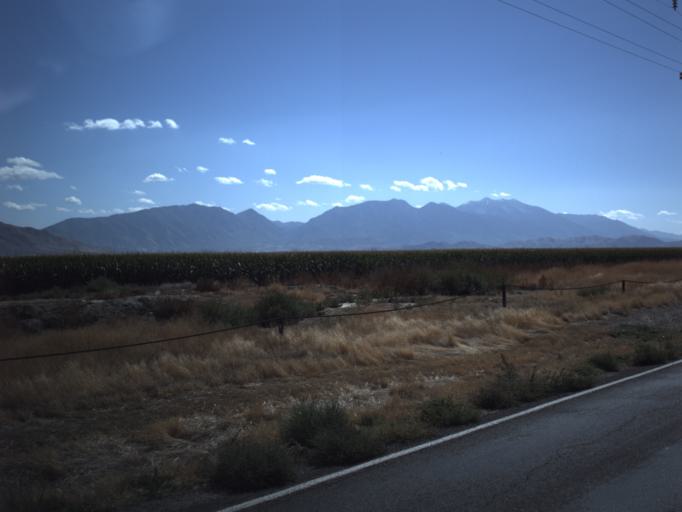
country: US
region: Utah
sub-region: Utah County
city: Genola
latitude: 40.1079
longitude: -111.9592
